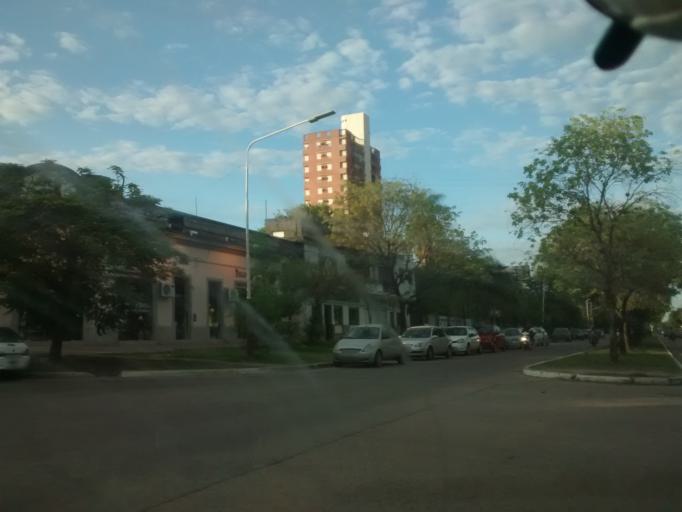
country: AR
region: Chaco
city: Resistencia
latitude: -27.4597
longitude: -58.9819
